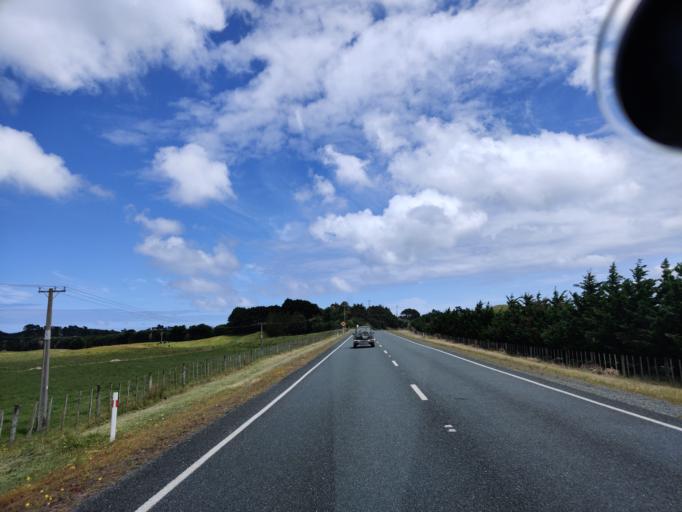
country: NZ
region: Northland
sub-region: Far North District
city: Kaitaia
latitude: -34.8967
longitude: 173.1707
